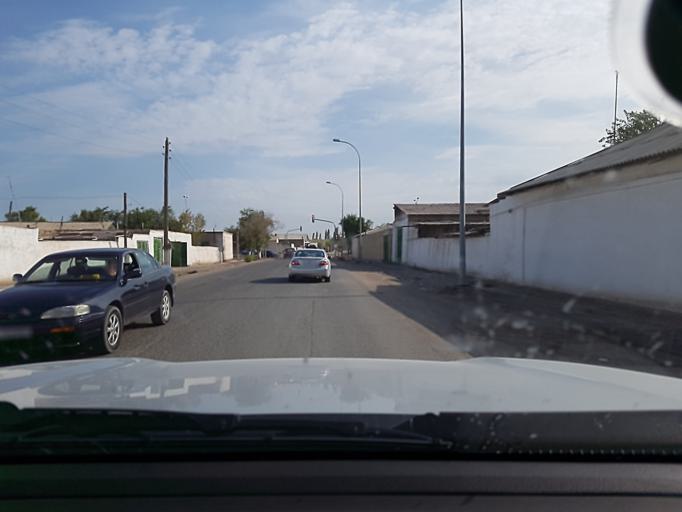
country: TM
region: Dasoguz
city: Koeneuergench
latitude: 42.3218
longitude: 59.1594
